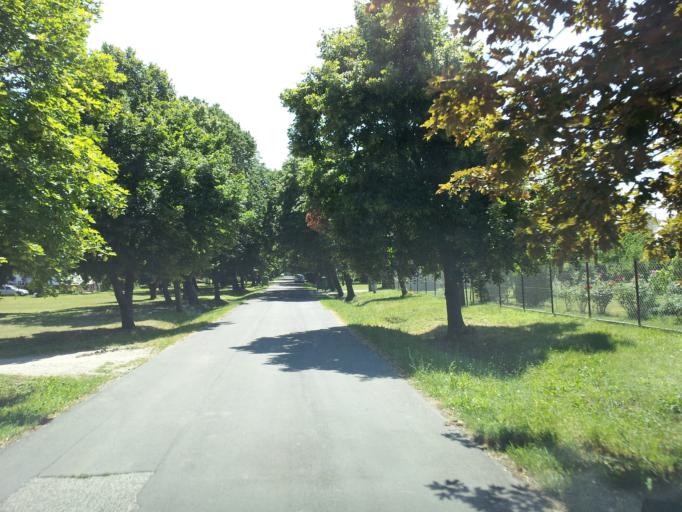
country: HU
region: Veszprem
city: Berhida
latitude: 47.1171
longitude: 18.1054
